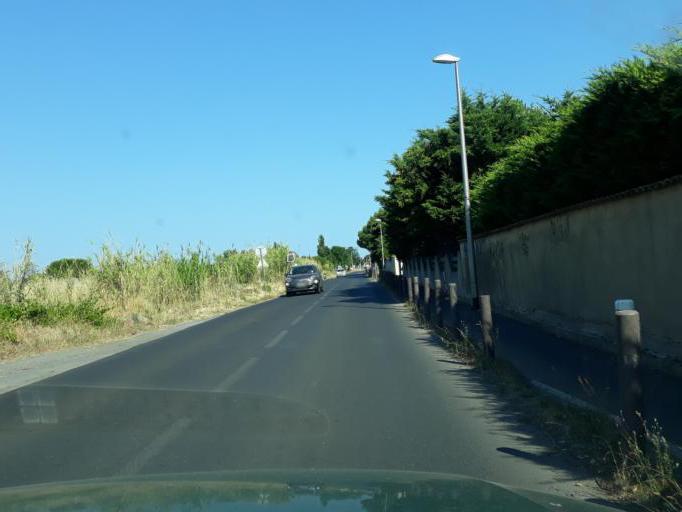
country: FR
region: Languedoc-Roussillon
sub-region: Departement de l'Herault
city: Agde
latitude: 43.2902
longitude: 3.4666
